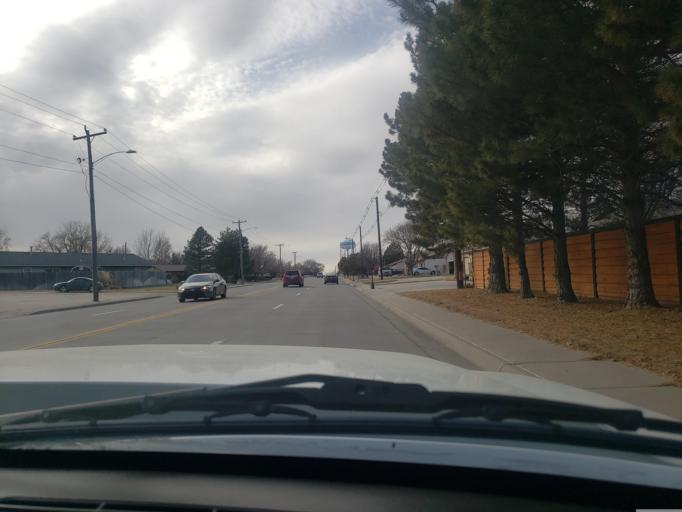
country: US
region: Kansas
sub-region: Finney County
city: Garden City
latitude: 37.9895
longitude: -100.8591
